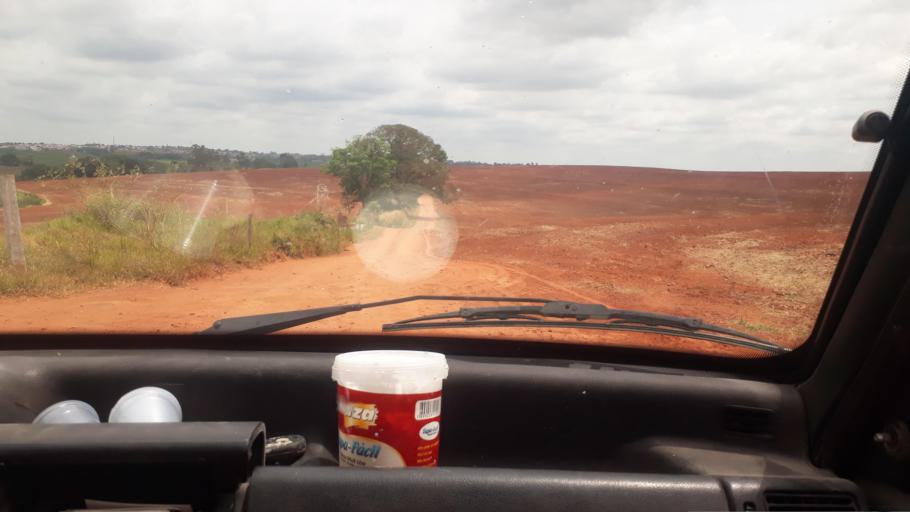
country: BR
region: Sao Paulo
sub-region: Regente Feijo
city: Regente Feijo
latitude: -22.2587
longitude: -51.3011
